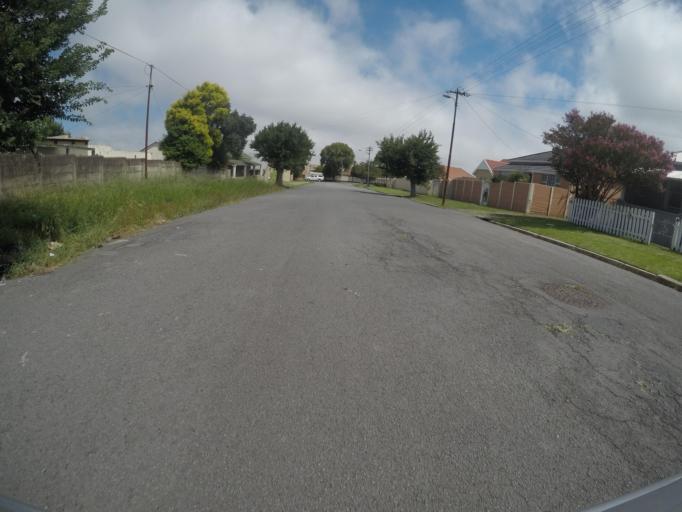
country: ZA
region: Eastern Cape
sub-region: Buffalo City Metropolitan Municipality
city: East London
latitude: -32.9797
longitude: 27.8900
